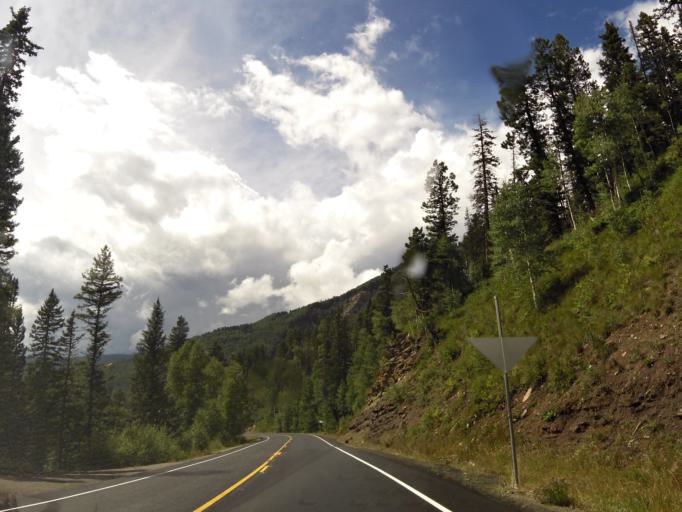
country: US
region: Colorado
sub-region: San Juan County
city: Silverton
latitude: 37.6807
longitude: -107.7868
